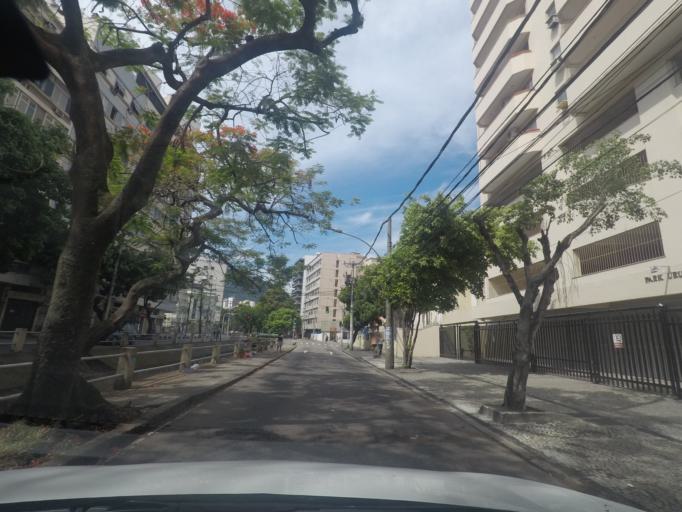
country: BR
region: Rio de Janeiro
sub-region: Rio De Janeiro
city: Rio de Janeiro
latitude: -22.9303
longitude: -43.2418
